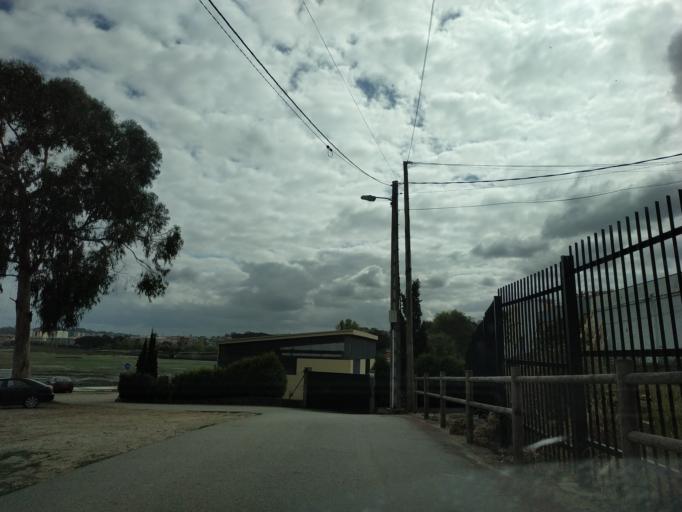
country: ES
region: Galicia
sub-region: Provincia da Coruna
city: Culleredo
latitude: 43.3273
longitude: -8.3807
